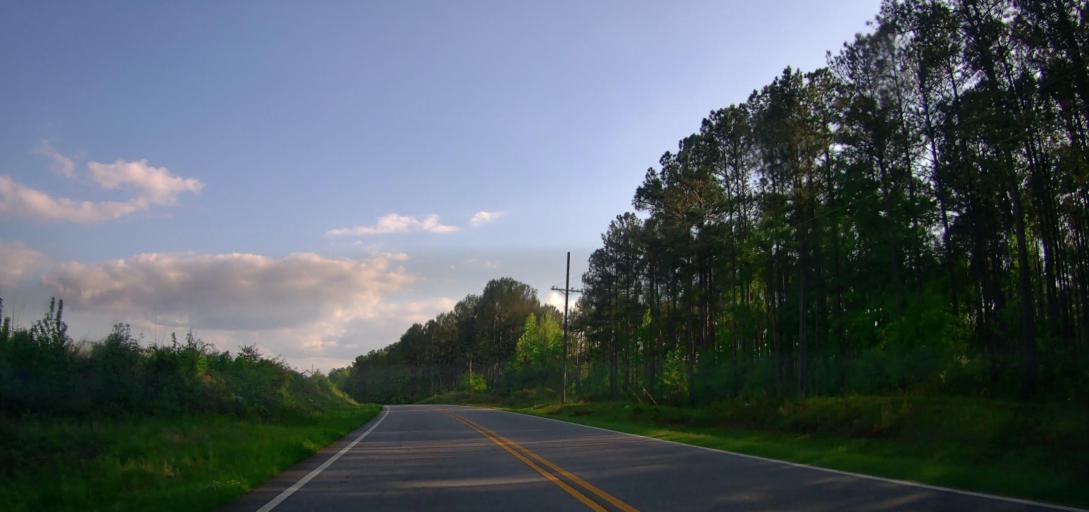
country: US
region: Georgia
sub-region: Putnam County
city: Eatonton
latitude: 33.2516
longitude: -83.3033
